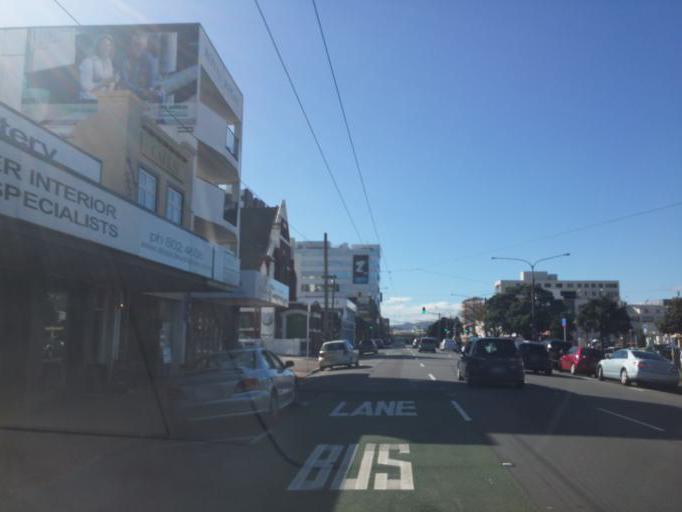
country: NZ
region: Wellington
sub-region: Wellington City
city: Wellington
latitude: -41.2965
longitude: 174.7823
